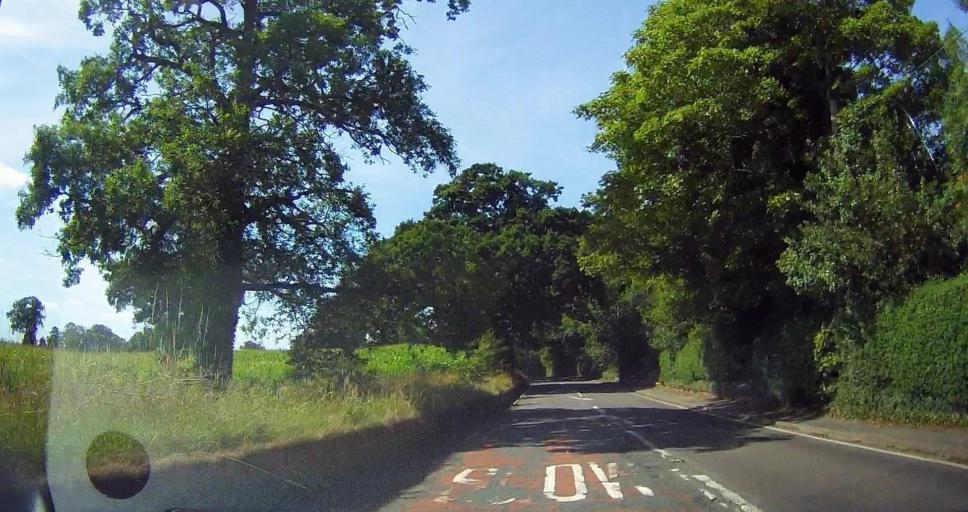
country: GB
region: England
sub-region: Shropshire
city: Market Drayton
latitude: 52.9576
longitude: -2.5068
